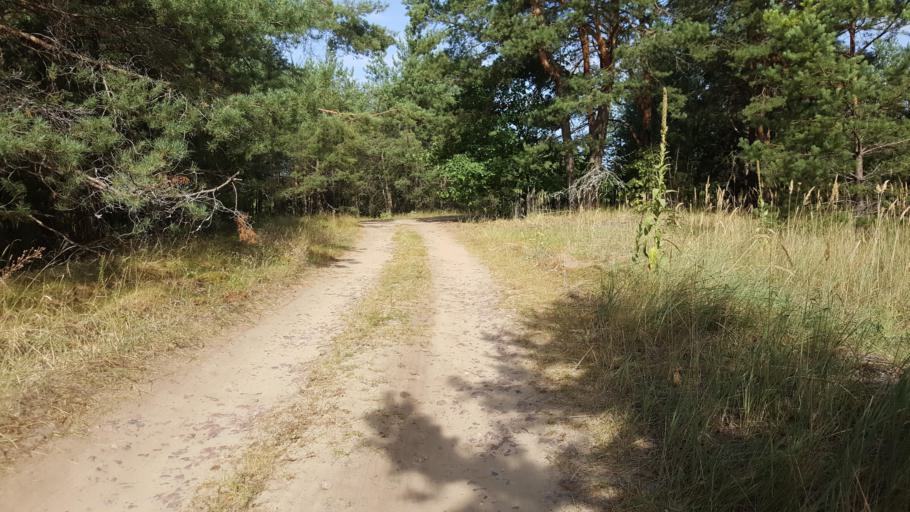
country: BY
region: Brest
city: Ivatsevichy
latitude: 52.7939
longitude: 25.5614
